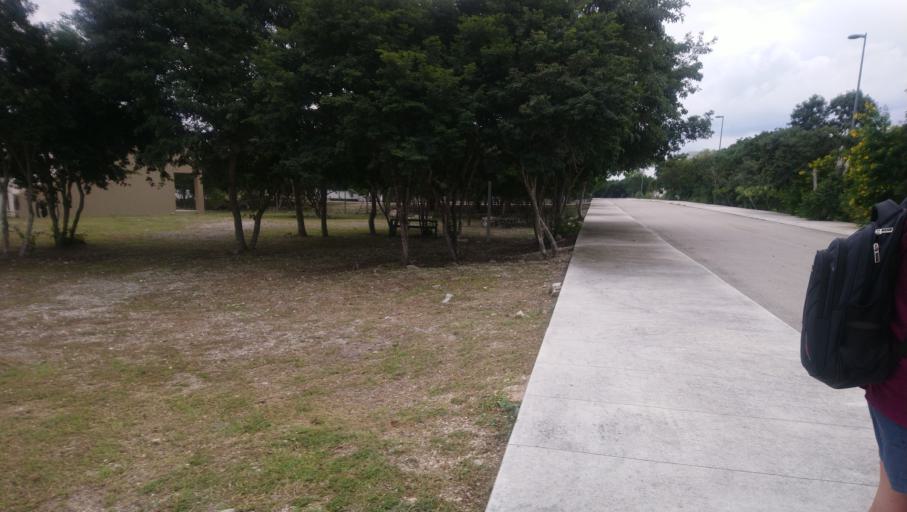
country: MX
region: Yucatan
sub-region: Merida
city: Sierra Papacal
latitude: 21.1297
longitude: -89.7819
